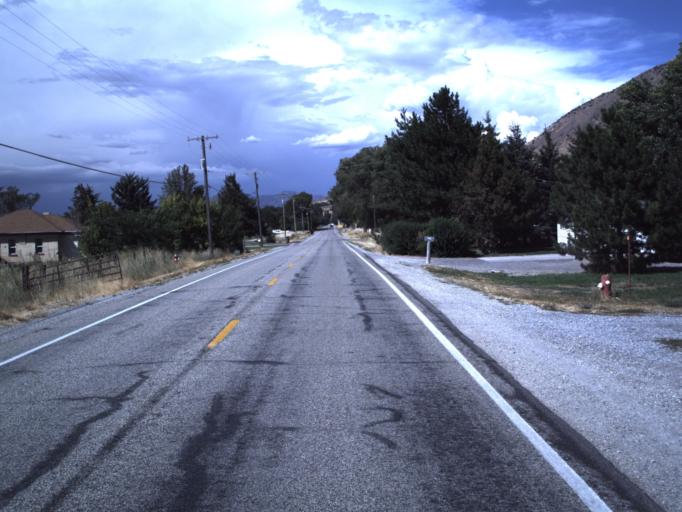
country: US
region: Utah
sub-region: Box Elder County
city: Elwood
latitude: 41.6979
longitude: -112.0901
